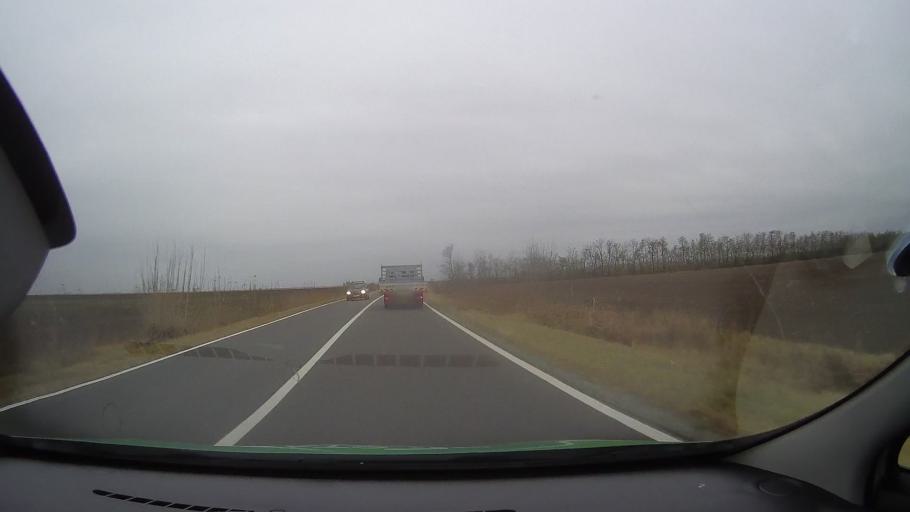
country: RO
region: Ialomita
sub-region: Comuna Gheorghe Lazar
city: Gheorghe Lazar
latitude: 44.6736
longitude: 27.4184
